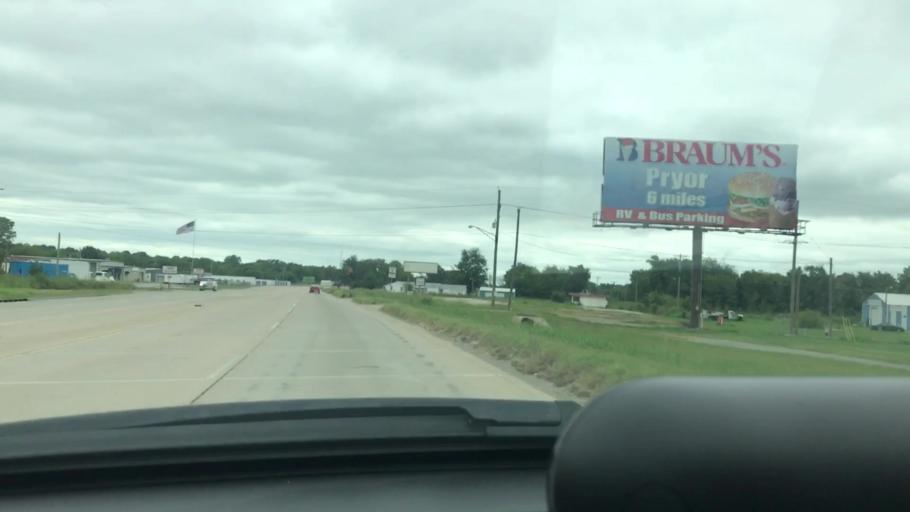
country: US
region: Oklahoma
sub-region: Mayes County
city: Chouteau
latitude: 36.1764
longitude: -95.3421
